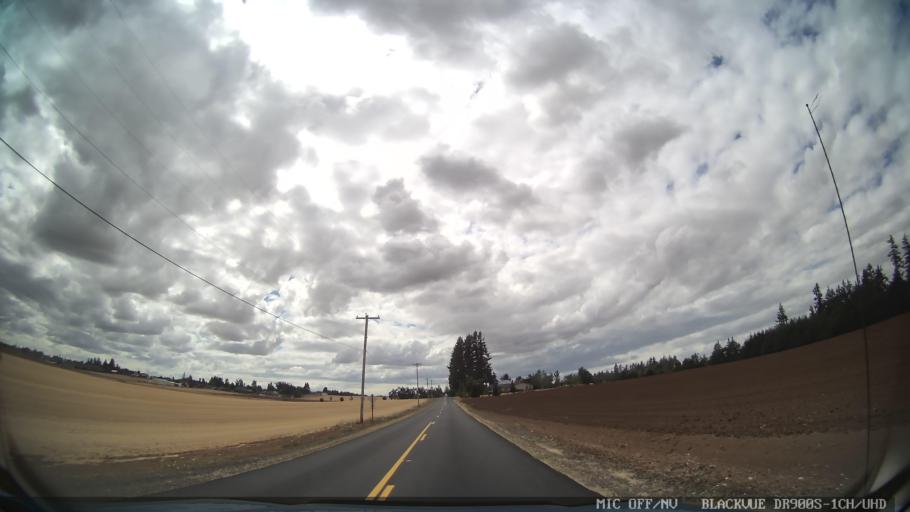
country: US
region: Oregon
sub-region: Marion County
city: Sublimity
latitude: 44.8405
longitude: -122.7759
